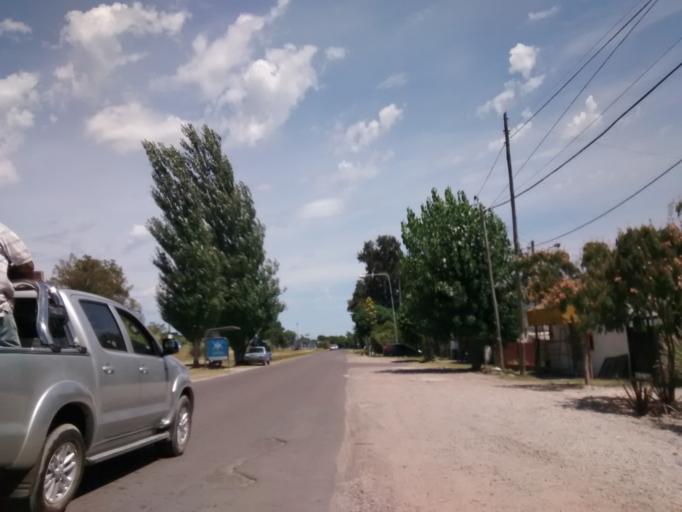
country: AR
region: Buenos Aires
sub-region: Partido de La Plata
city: La Plata
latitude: -34.8686
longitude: -58.0351
